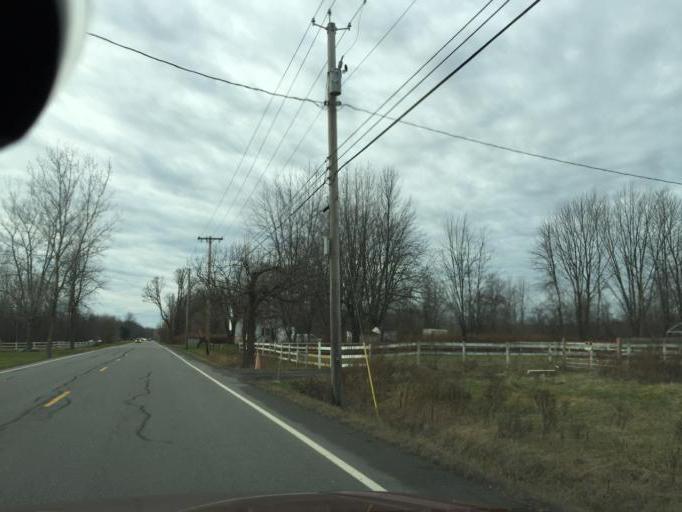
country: US
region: New York
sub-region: Monroe County
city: Scottsville
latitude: 43.0912
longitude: -77.7123
